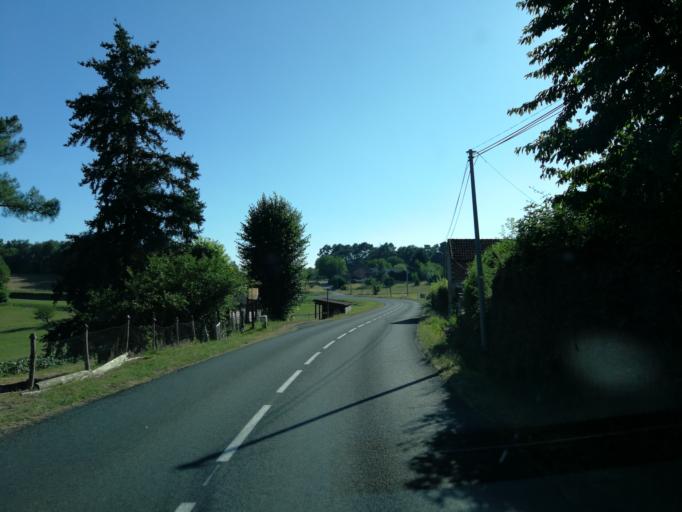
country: FR
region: Midi-Pyrenees
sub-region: Departement du Lot
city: Salviac
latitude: 44.6122
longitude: 1.2033
